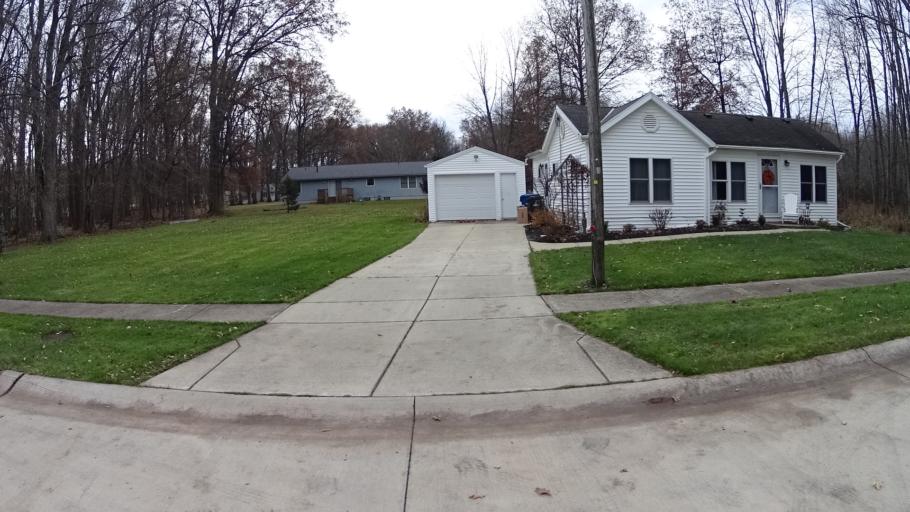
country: US
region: Ohio
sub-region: Lorain County
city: Sheffield
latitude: 41.3879
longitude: -82.0651
